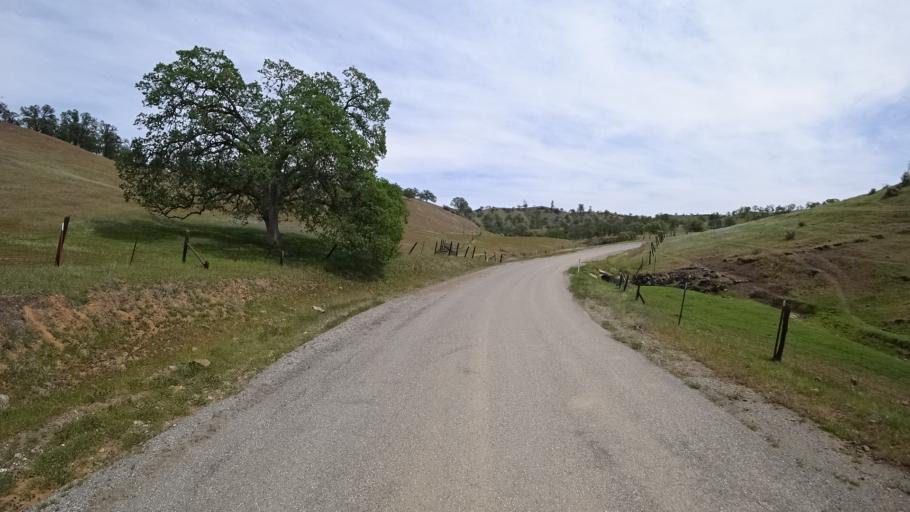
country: US
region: California
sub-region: Glenn County
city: Willows
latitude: 39.6273
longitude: -122.5908
